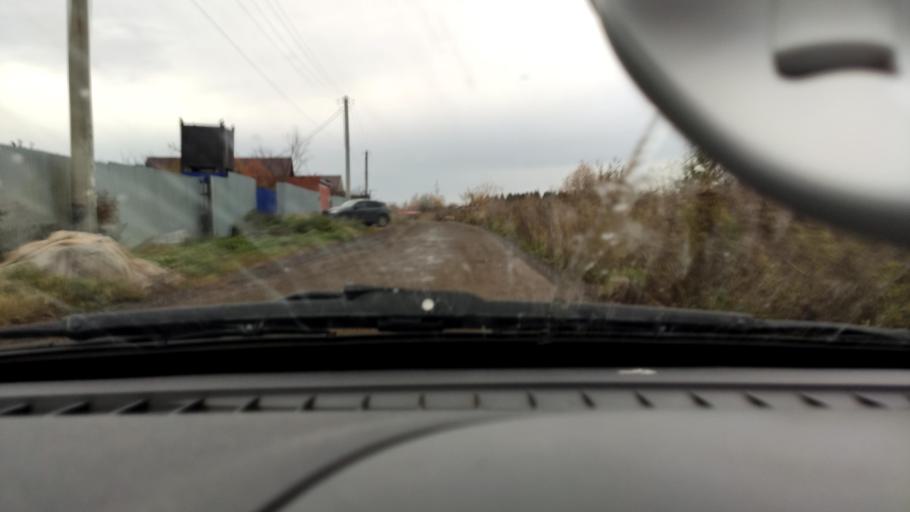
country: RU
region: Perm
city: Kondratovo
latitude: 57.9542
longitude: 56.1655
